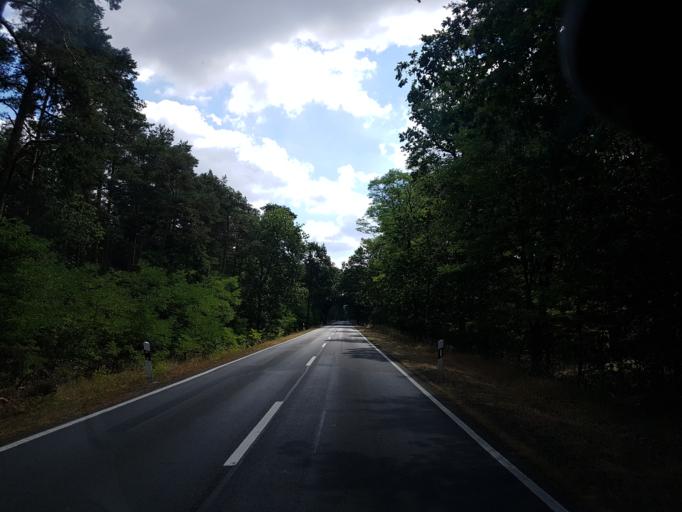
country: DE
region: Brandenburg
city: Drebkau
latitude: 51.6642
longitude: 14.1912
